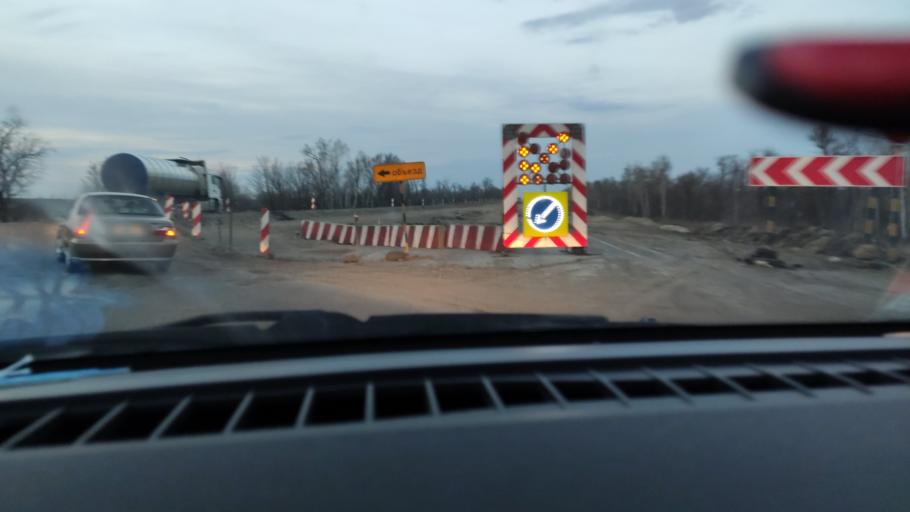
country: RU
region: Saratov
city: Sinodskoye
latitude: 52.0212
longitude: 46.7068
